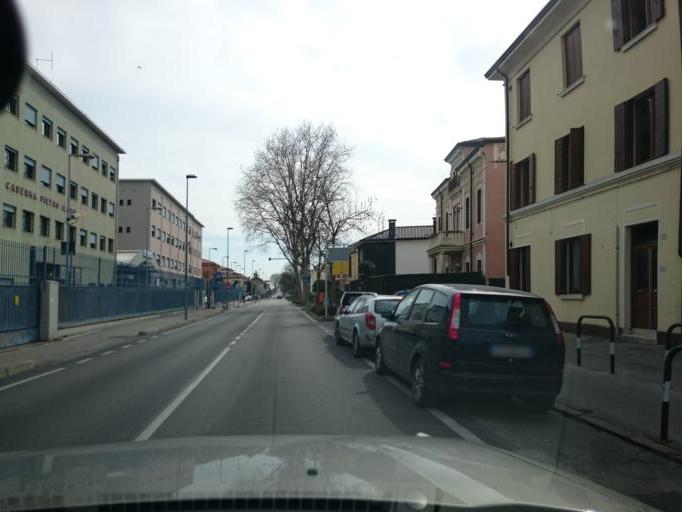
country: IT
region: Veneto
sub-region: Provincia di Padova
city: Padova
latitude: 45.3911
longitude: 11.8793
